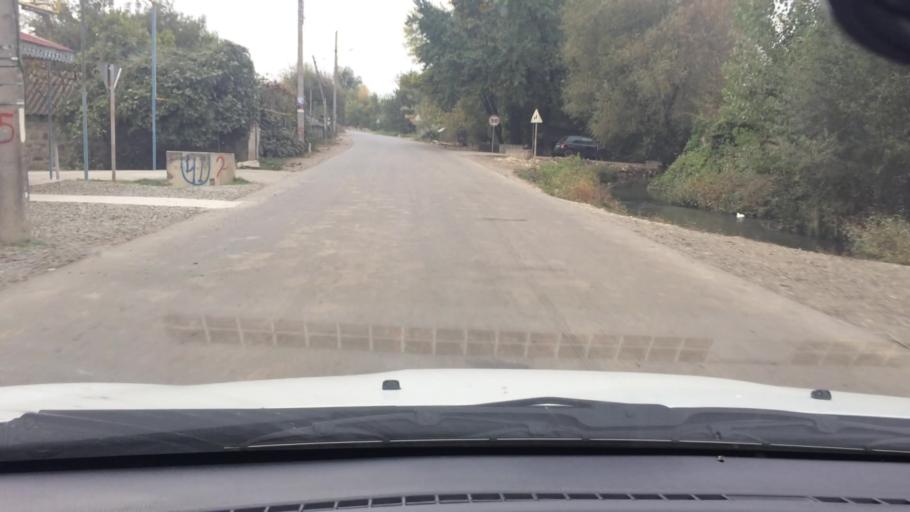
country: AM
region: Tavush
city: Berdavan
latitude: 41.3500
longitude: 44.9727
